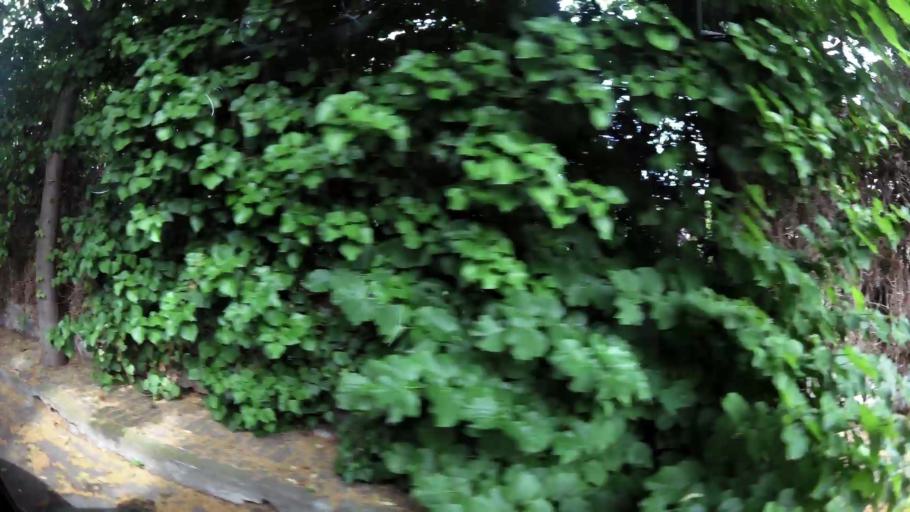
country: GR
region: Central Macedonia
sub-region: Nomos Thessalonikis
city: Panorama
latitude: 40.5933
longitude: 23.0099
